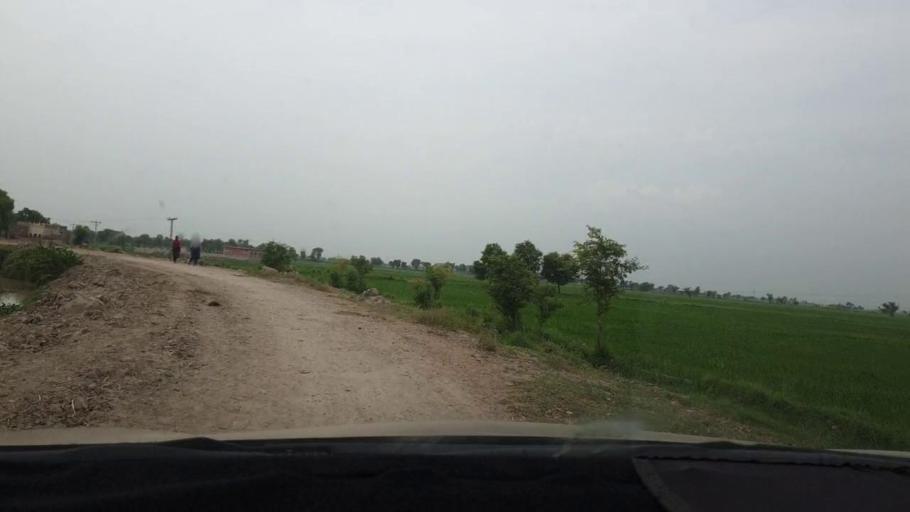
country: PK
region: Sindh
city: Ratodero
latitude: 27.7582
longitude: 68.3094
